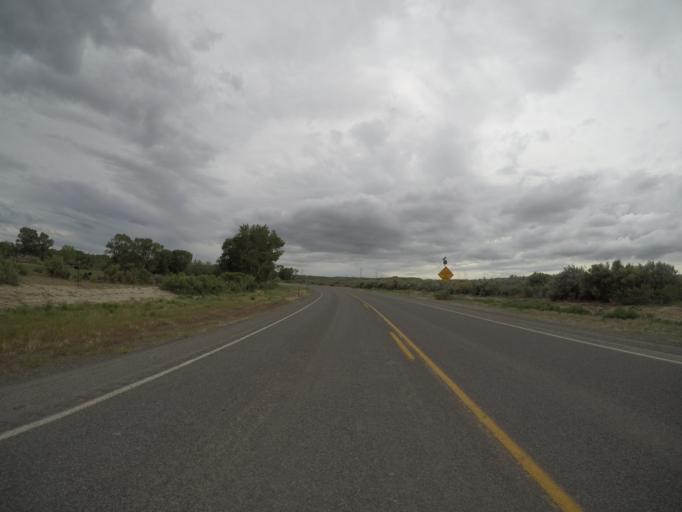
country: US
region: Wyoming
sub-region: Big Horn County
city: Lovell
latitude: 44.8654
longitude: -108.3303
